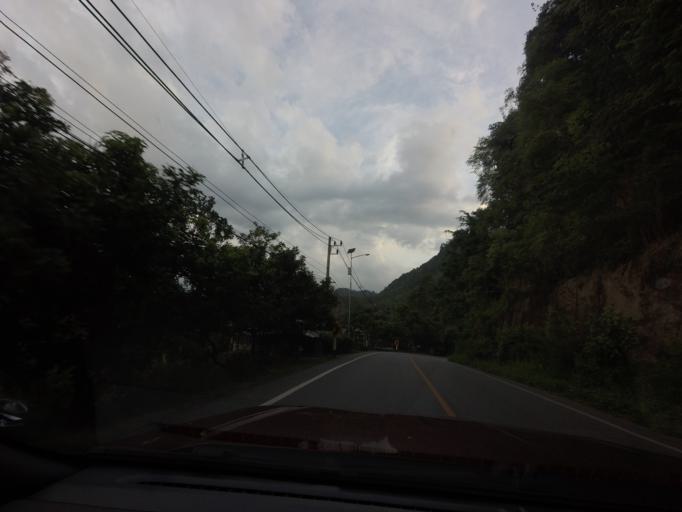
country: TH
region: Yala
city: Than To
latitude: 6.0106
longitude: 101.1960
